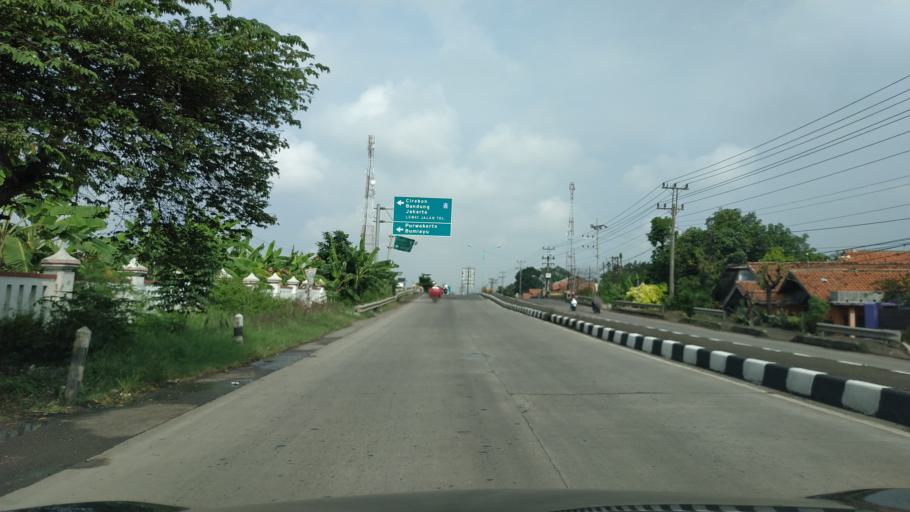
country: ID
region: Central Java
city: Ketanggungan
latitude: -6.8720
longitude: 108.8888
